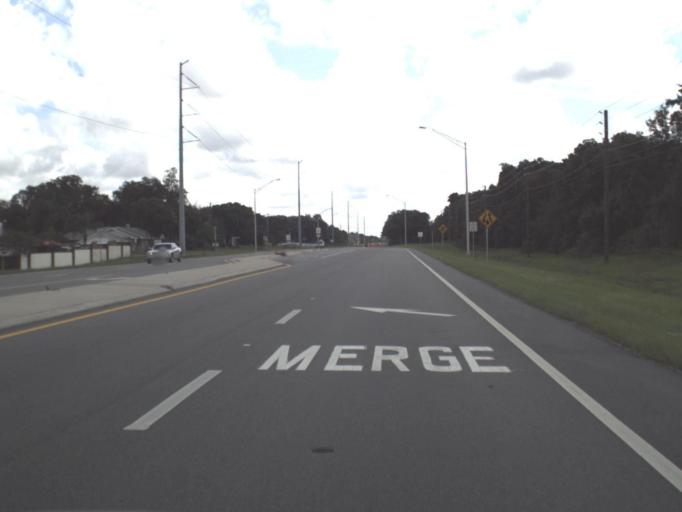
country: US
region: Florida
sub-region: Polk County
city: Gibsonia
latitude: 28.1077
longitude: -81.9337
